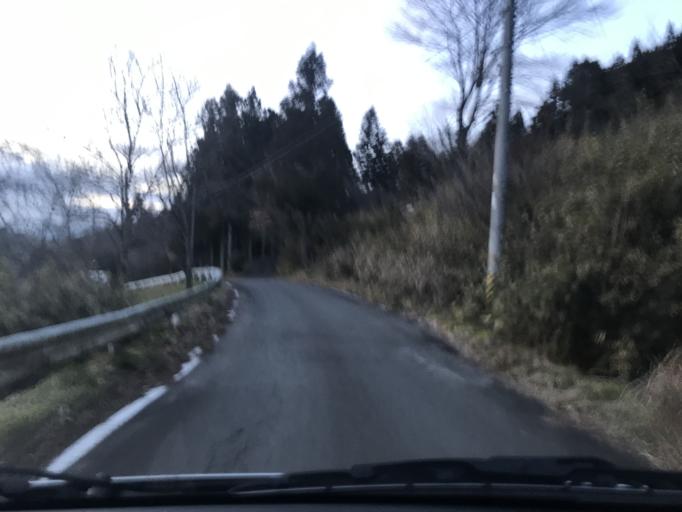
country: JP
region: Iwate
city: Ichinoseki
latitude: 38.8325
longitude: 141.0880
